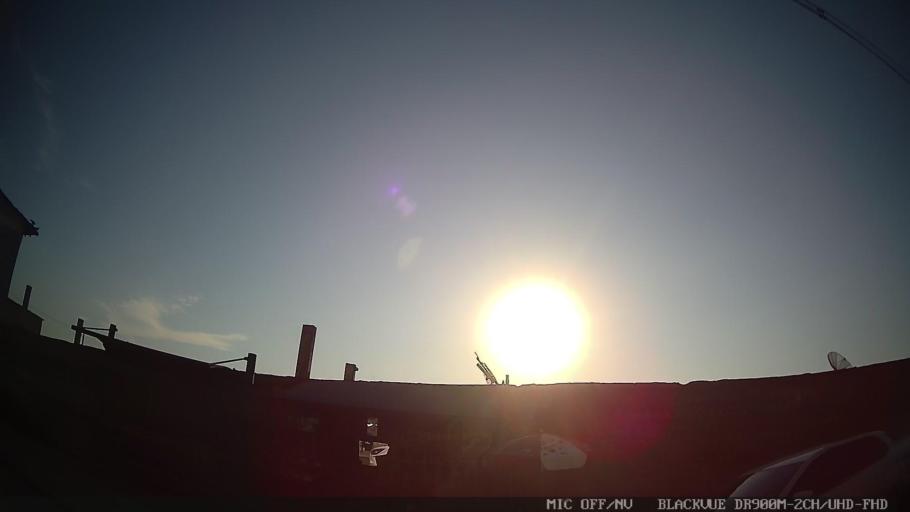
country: BR
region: Sao Paulo
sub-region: Guaruja
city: Guaruja
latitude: -23.9794
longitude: -46.2607
